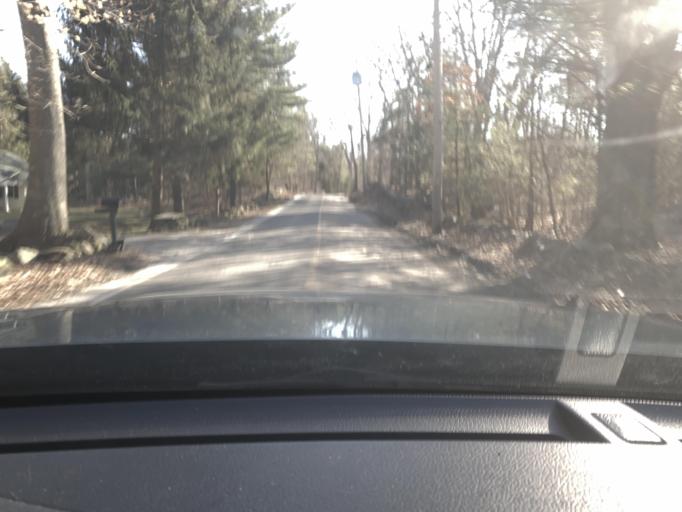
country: US
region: Massachusetts
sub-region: Middlesex County
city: Sherborn
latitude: 42.2213
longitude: -71.3752
